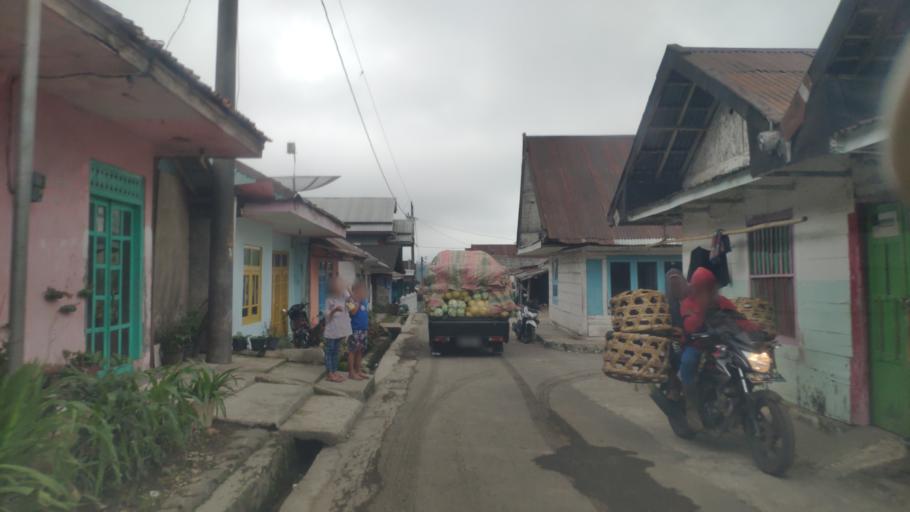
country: ID
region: Central Java
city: Wonosobo
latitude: -7.2326
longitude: 109.7165
